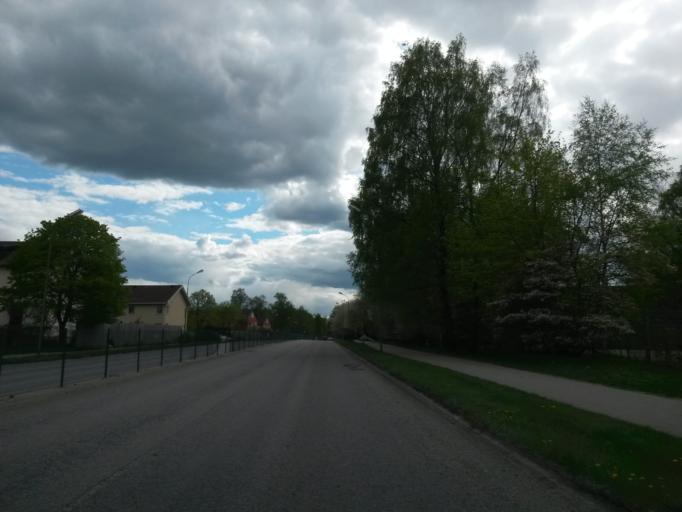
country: SE
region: Vaestra Goetaland
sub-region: Boras Kommun
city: Boras
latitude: 57.7525
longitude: 12.9473
